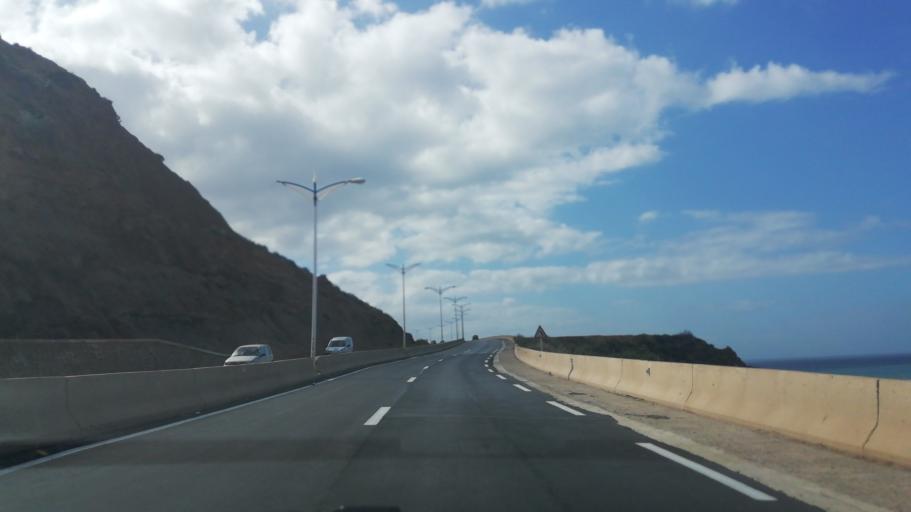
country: DZ
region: Mostaganem
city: Mostaganem
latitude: 36.0106
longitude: 0.1279
